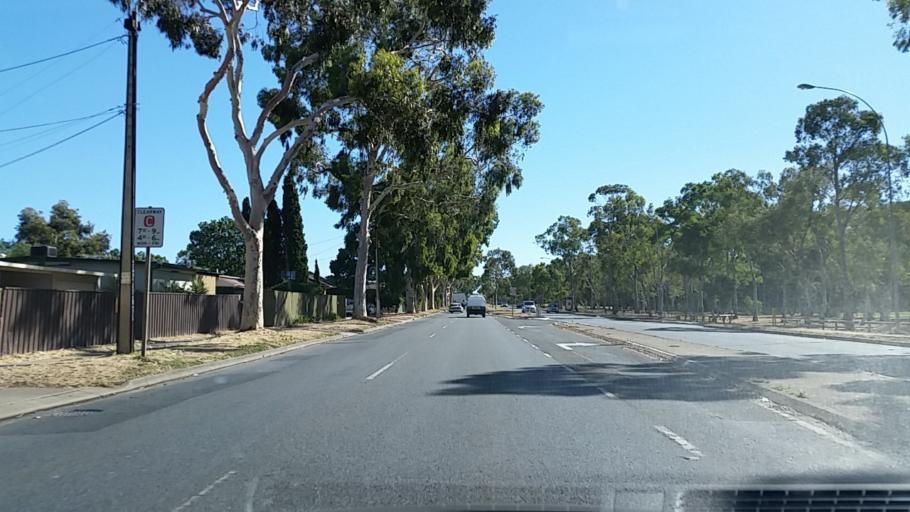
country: AU
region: South Australia
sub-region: Salisbury
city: Ingle Farm
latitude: -34.8109
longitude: 138.6455
